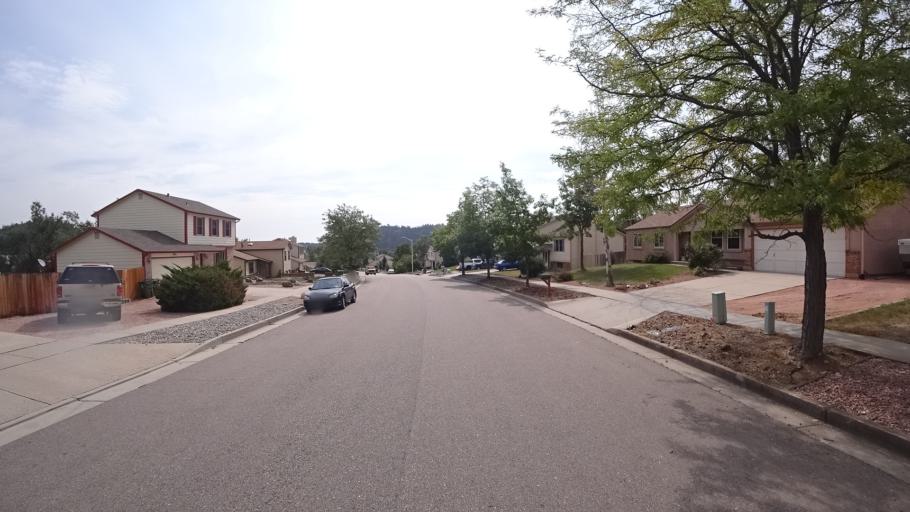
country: US
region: Colorado
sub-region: El Paso County
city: Colorado Springs
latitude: 38.8906
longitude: -104.7911
